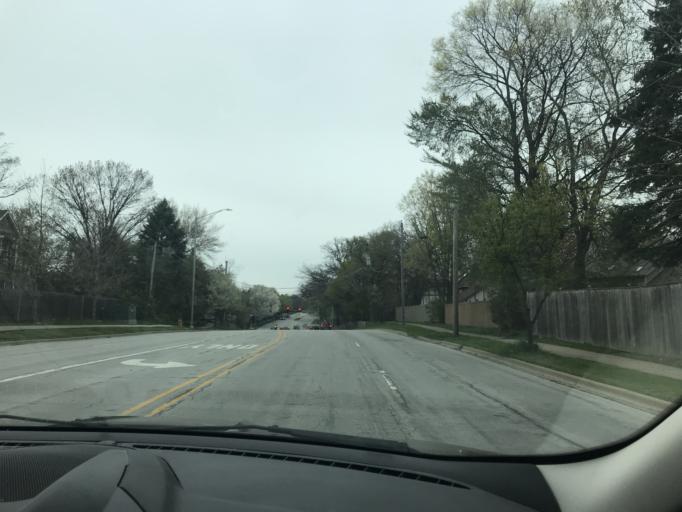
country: US
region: Illinois
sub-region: DuPage County
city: Naperville
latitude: 41.7389
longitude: -88.1177
